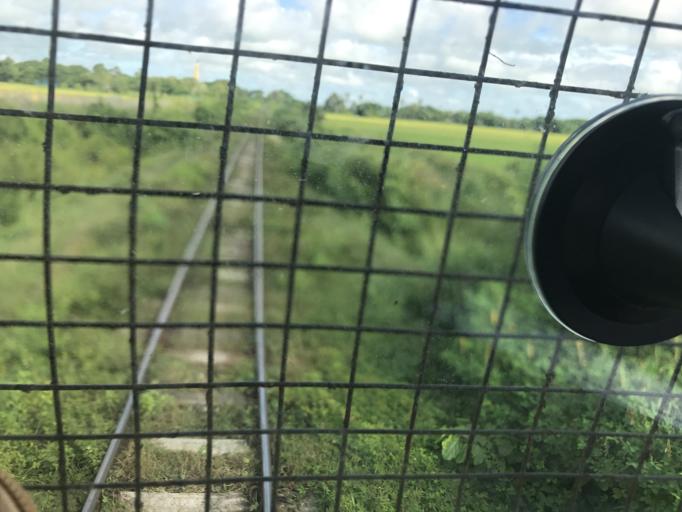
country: MM
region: Bago
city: Letpandan
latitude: 18.0941
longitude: 95.6807
